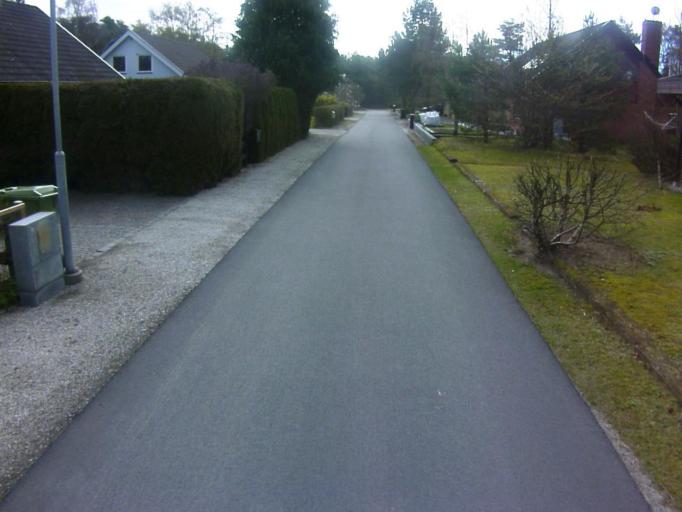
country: SE
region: Skane
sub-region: Kavlinge Kommun
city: Hofterup
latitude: 55.7991
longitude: 12.9841
